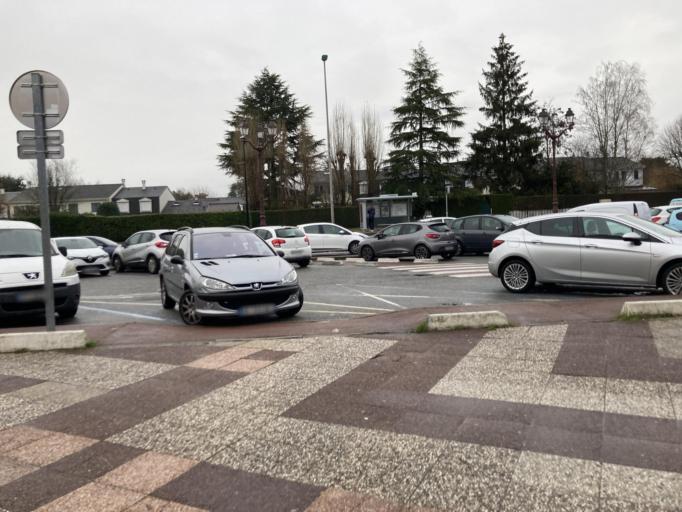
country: FR
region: Ile-de-France
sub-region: Departement des Yvelines
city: Elancourt
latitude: 48.7702
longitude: 1.9694
